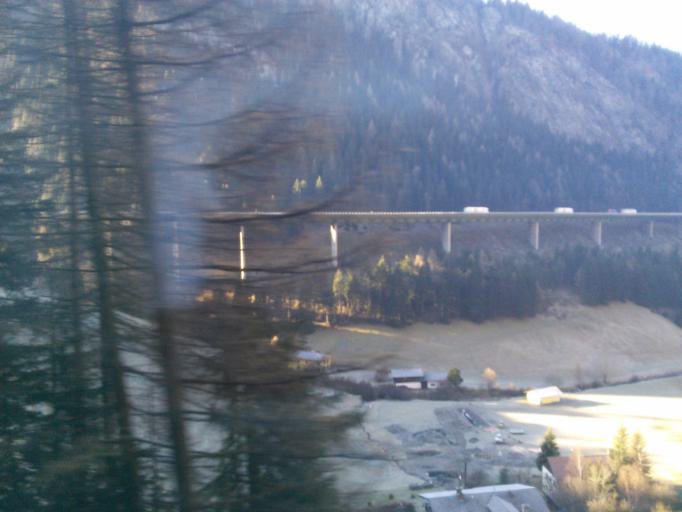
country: AT
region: Tyrol
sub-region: Politischer Bezirk Innsbruck Land
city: Gries am Brenner
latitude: 47.0270
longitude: 11.5022
